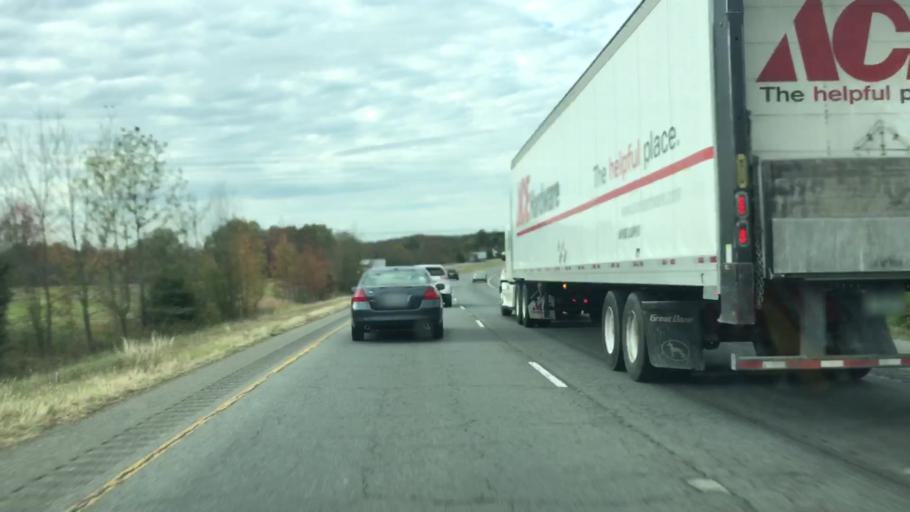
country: US
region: Arkansas
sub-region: Faulkner County
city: Conway
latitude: 35.1250
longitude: -92.5083
